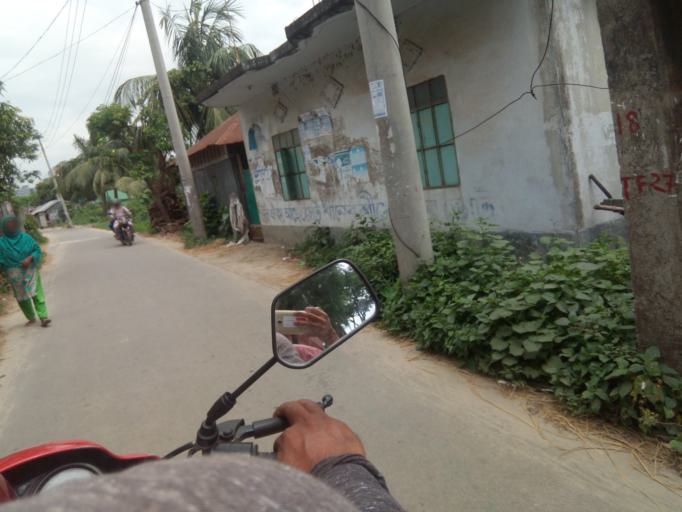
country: BD
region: Dhaka
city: Paltan
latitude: 23.7358
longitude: 90.4899
